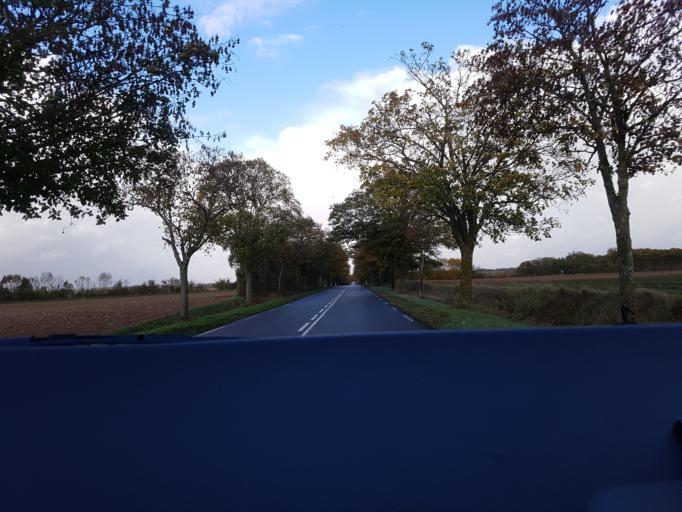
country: FR
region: Poitou-Charentes
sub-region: Departement des Deux-Sevres
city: Brioux-sur-Boutonne
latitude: 46.0977
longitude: -0.2755
